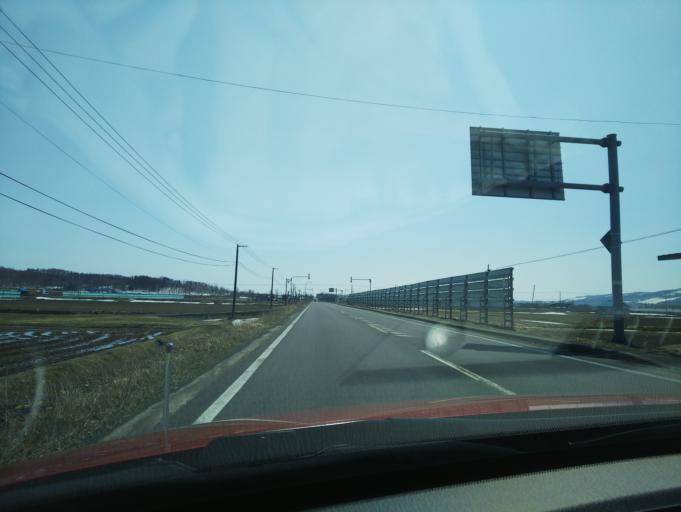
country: JP
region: Hokkaido
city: Nayoro
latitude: 44.2679
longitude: 142.3947
